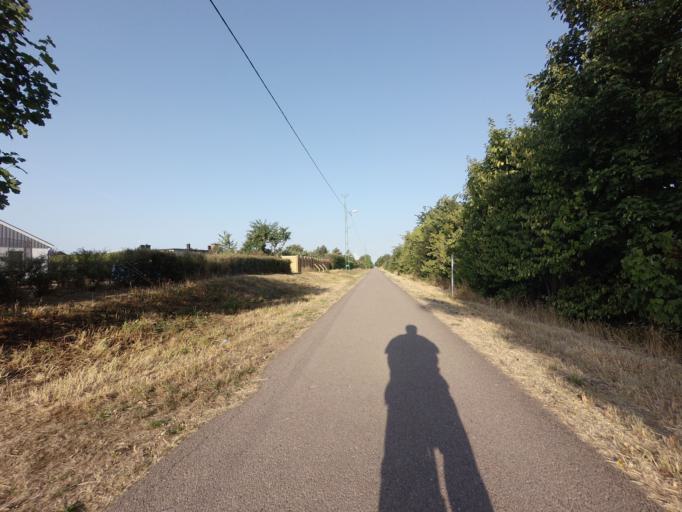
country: SE
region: Skane
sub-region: Landskrona
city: Asmundtorp
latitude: 55.8835
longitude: 12.9389
